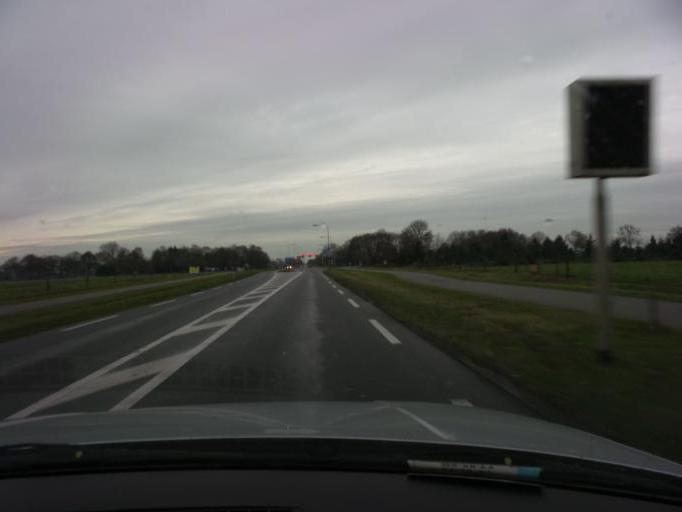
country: NL
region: Overijssel
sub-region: Gemeente Dalfsen
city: Dalfsen
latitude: 52.5286
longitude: 6.2646
